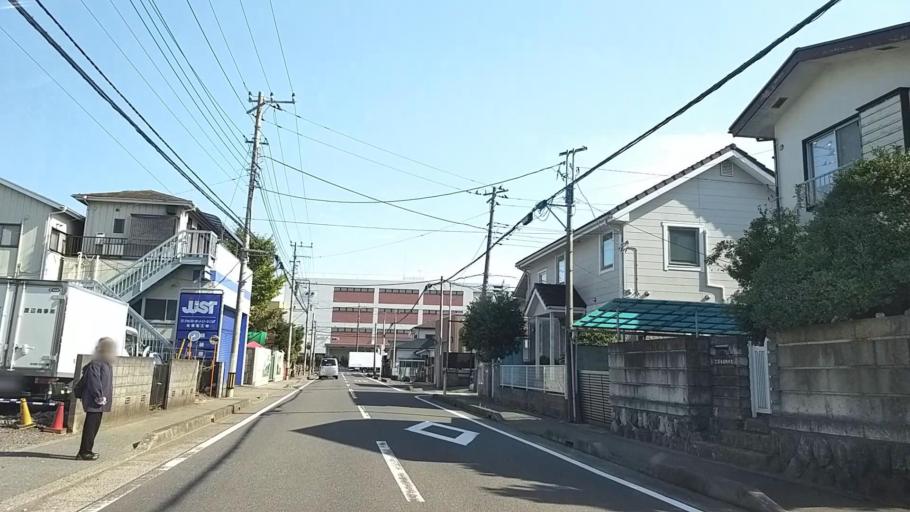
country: JP
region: Kanagawa
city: Atsugi
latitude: 35.4456
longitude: 139.3764
